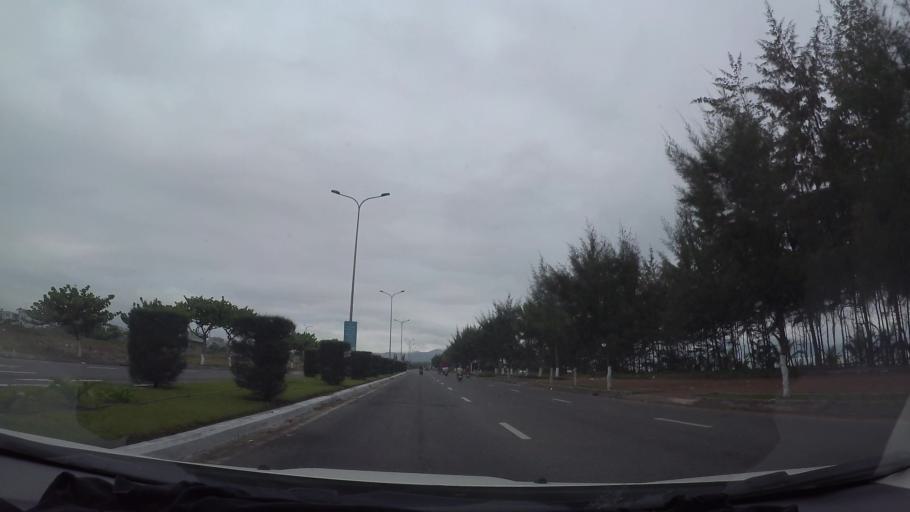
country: VN
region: Da Nang
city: Lien Chieu
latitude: 16.0900
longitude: 108.1526
